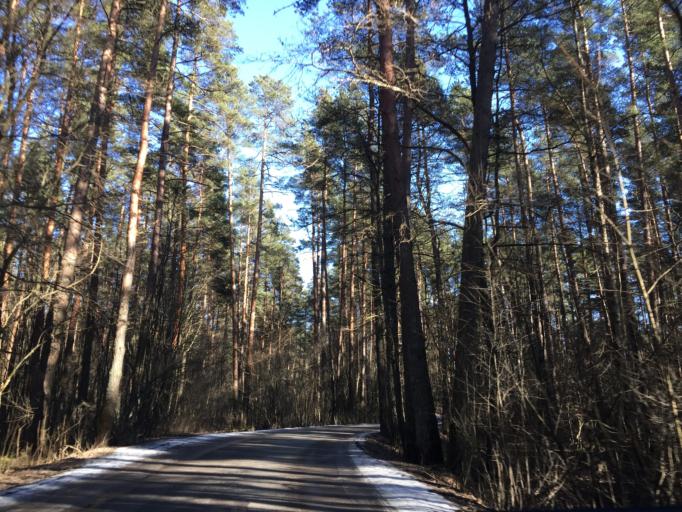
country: LV
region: Marupe
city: Marupe
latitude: 56.9660
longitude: 23.9933
